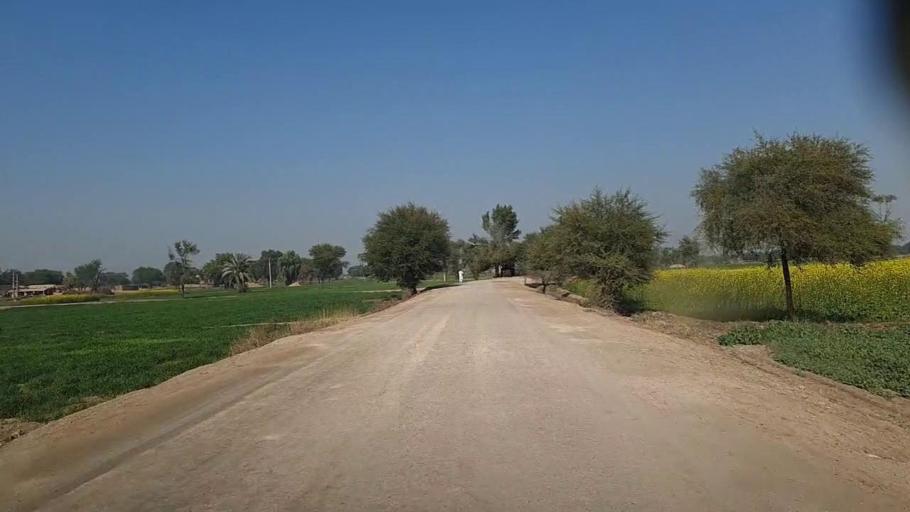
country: PK
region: Sindh
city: Khairpur
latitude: 27.9943
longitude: 69.8476
